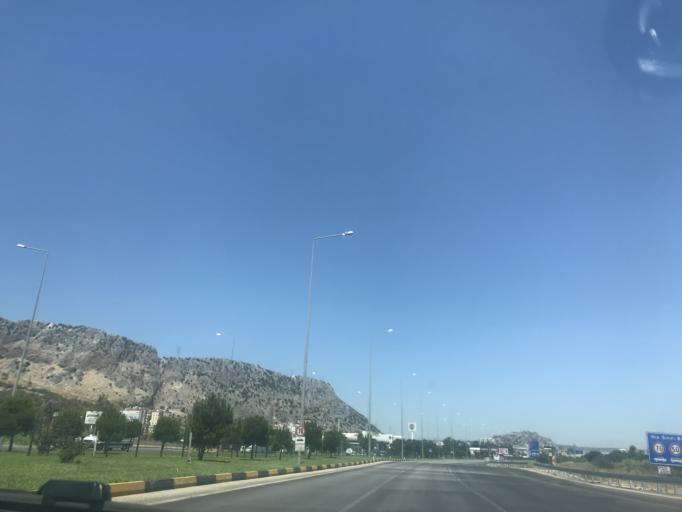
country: TR
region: Antalya
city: Cakirlar
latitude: 36.8367
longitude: 30.5959
